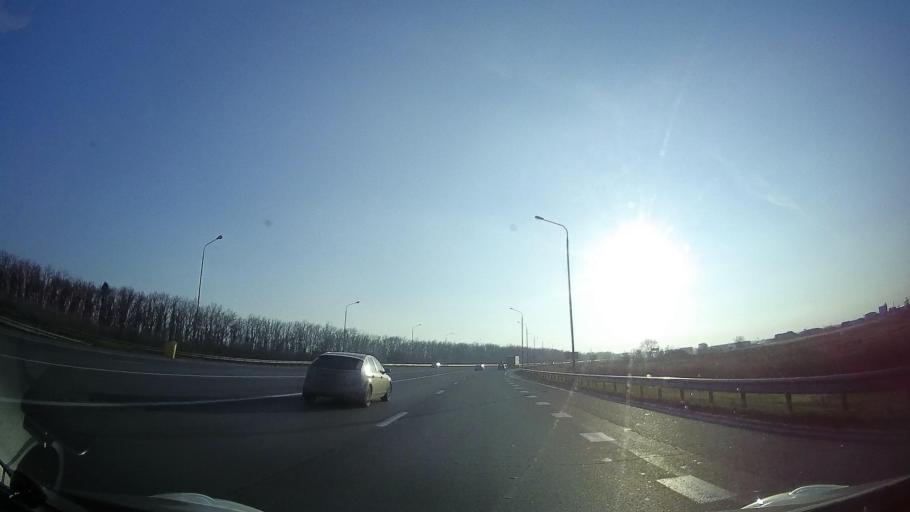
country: RU
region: Rostov
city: Ol'ginskaya
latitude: 47.1277
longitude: 39.8747
